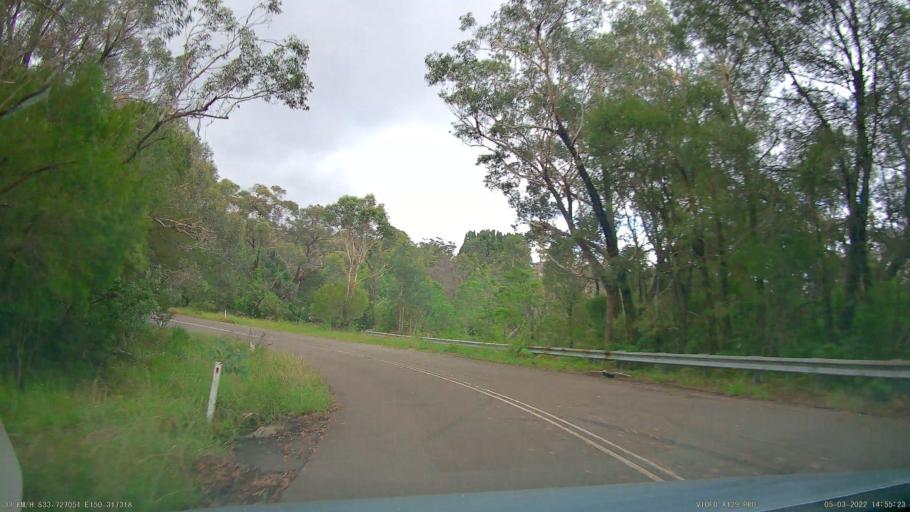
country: AU
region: New South Wales
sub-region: Blue Mountains Municipality
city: Katoomba
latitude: -33.7269
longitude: 150.3174
